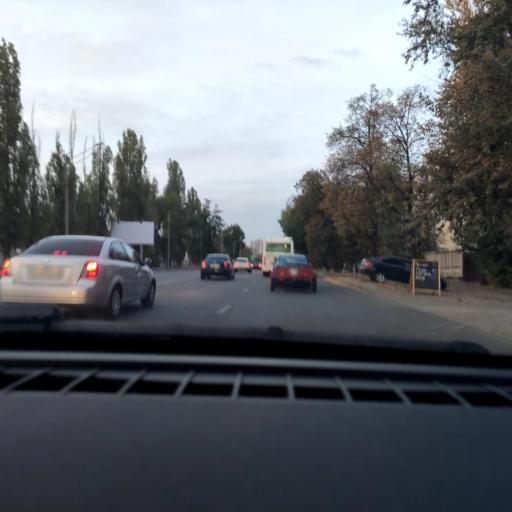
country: RU
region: Voronezj
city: Voronezh
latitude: 51.6546
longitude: 39.2731
